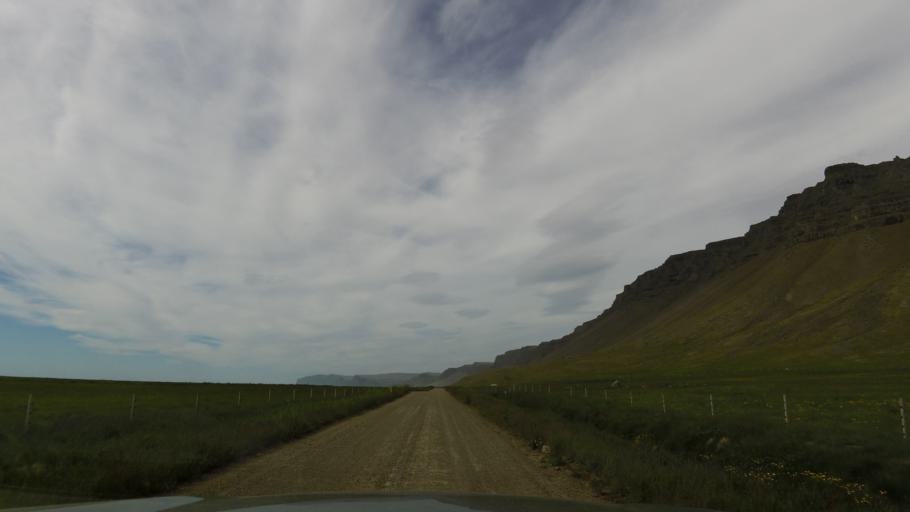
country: IS
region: West
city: Olafsvik
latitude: 65.4788
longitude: -24.0115
